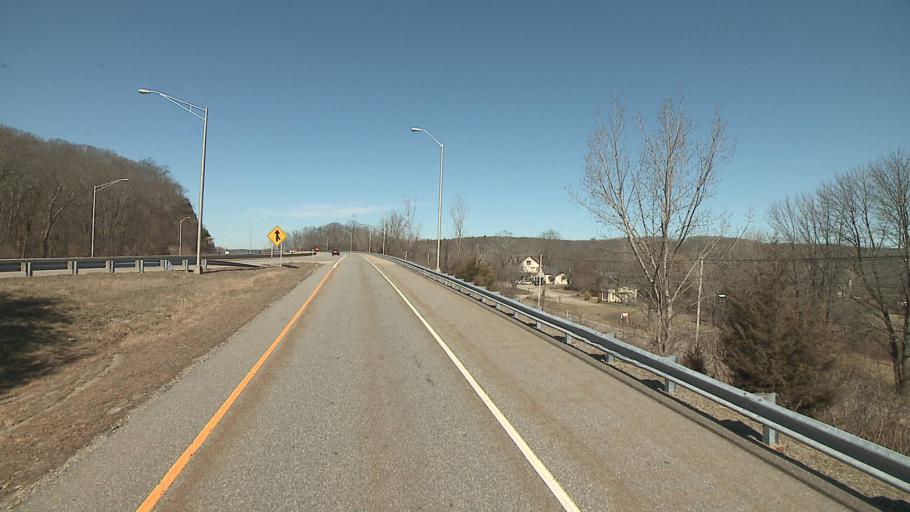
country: US
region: Connecticut
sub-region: New London County
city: Norwich
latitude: 41.5548
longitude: -72.1173
